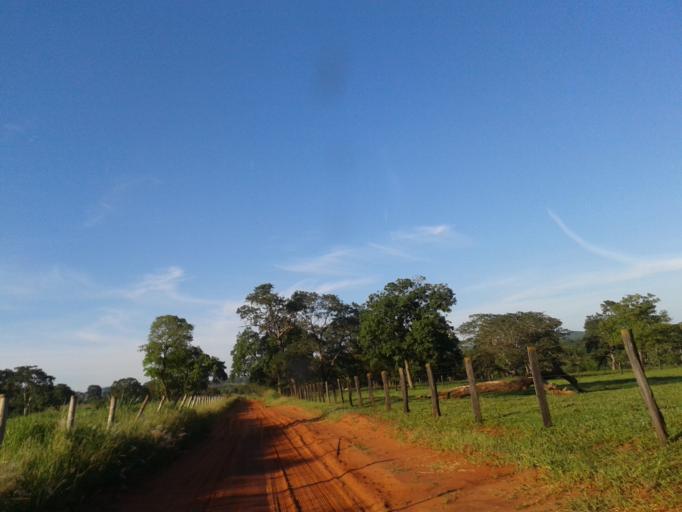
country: BR
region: Minas Gerais
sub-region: Santa Vitoria
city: Santa Vitoria
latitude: -18.9290
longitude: -49.8527
